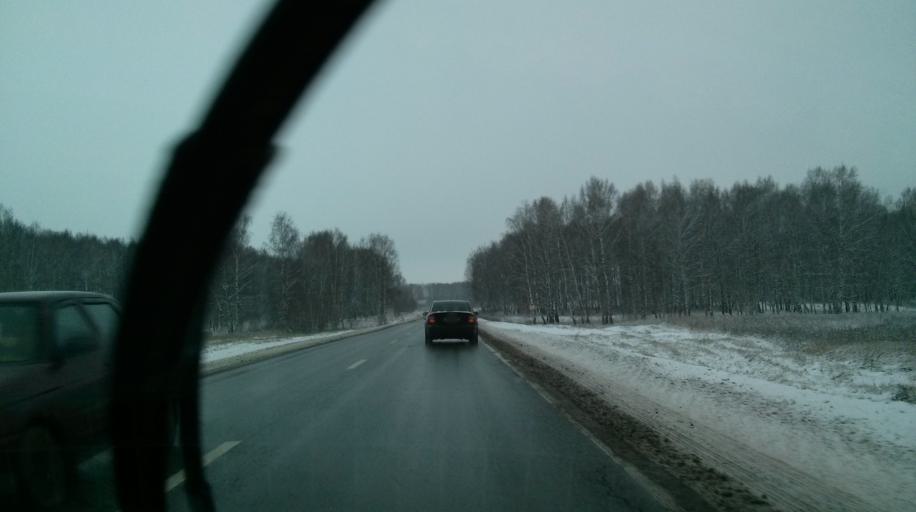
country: RU
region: Nizjnij Novgorod
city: Bogorodsk
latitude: 56.0736
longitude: 43.4576
